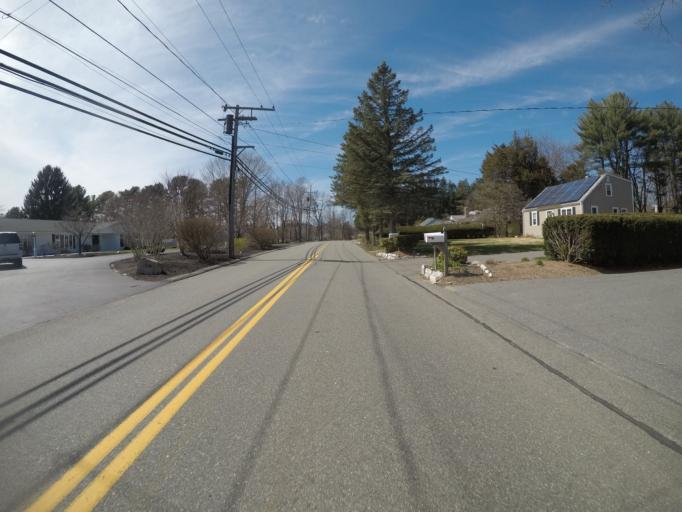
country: US
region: Massachusetts
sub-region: Bristol County
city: Easton
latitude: 42.0246
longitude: -71.0813
